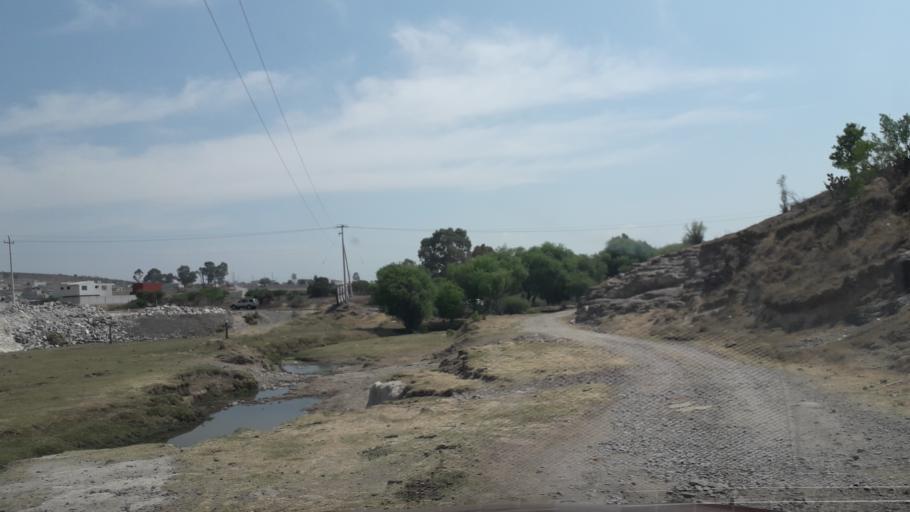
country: MX
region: Puebla
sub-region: Puebla
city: San Andres Azumiatla
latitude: 18.9252
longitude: -98.2549
